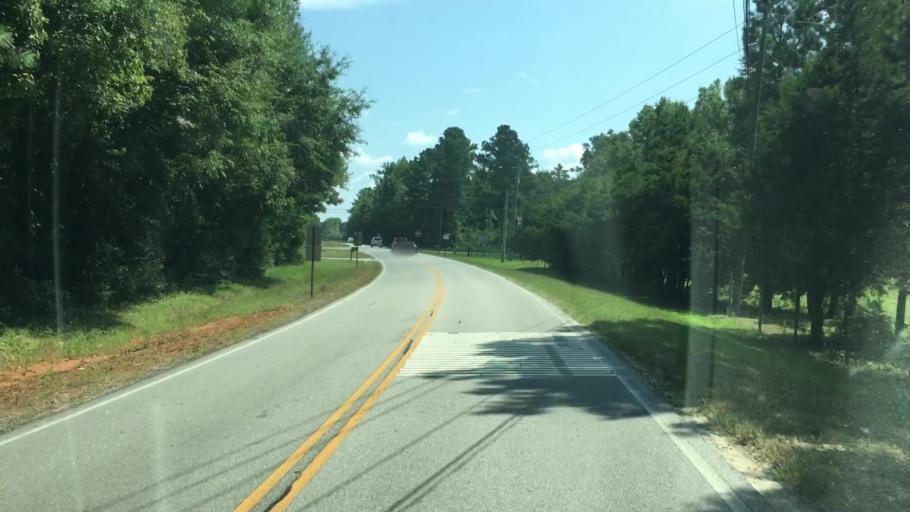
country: US
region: Georgia
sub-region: Oconee County
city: Watkinsville
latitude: 33.8443
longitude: -83.4484
